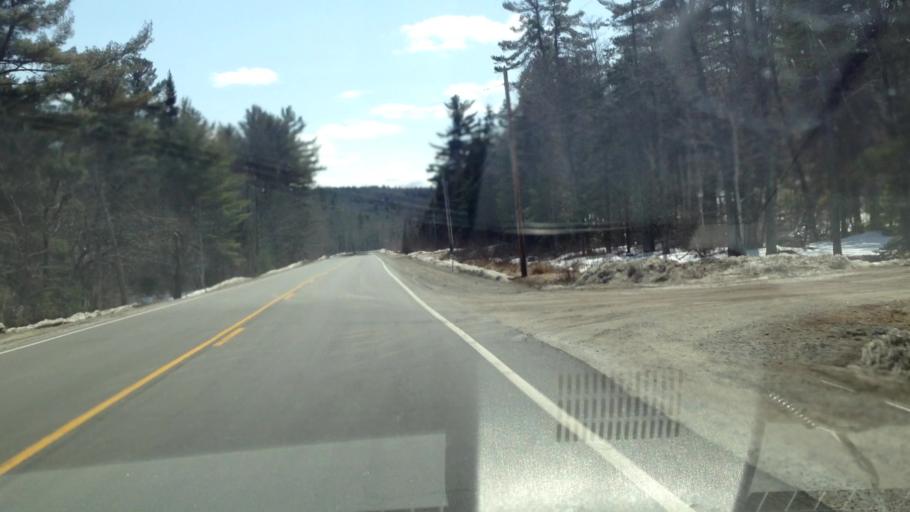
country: US
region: New Hampshire
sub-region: Merrimack County
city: Wilmot
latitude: 43.4729
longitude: -71.9633
